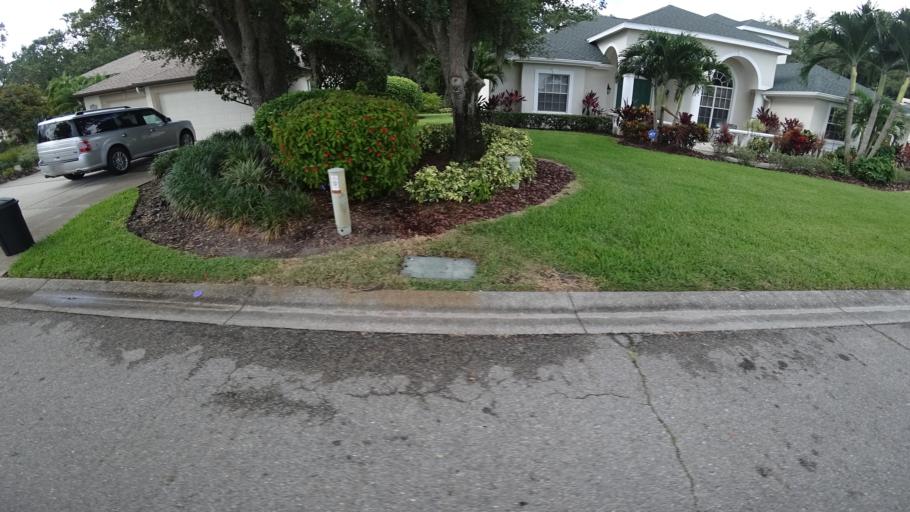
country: US
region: Florida
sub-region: Sarasota County
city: The Meadows
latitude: 27.4159
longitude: -82.4303
